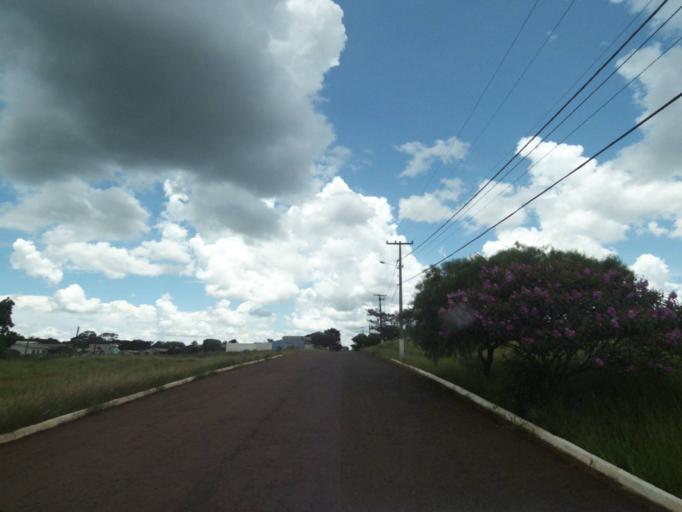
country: BR
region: Parana
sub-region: Guaraniacu
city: Guaraniacu
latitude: -25.1047
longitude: -52.8575
